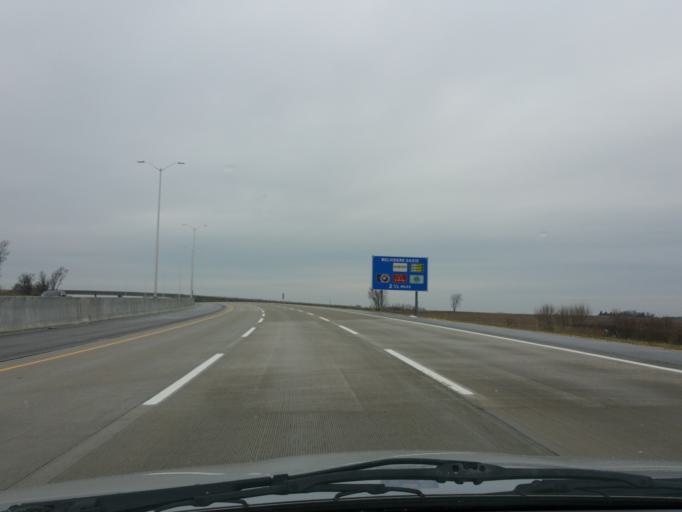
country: US
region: Illinois
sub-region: Boone County
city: Belvidere
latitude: 42.2328
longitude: -88.7822
